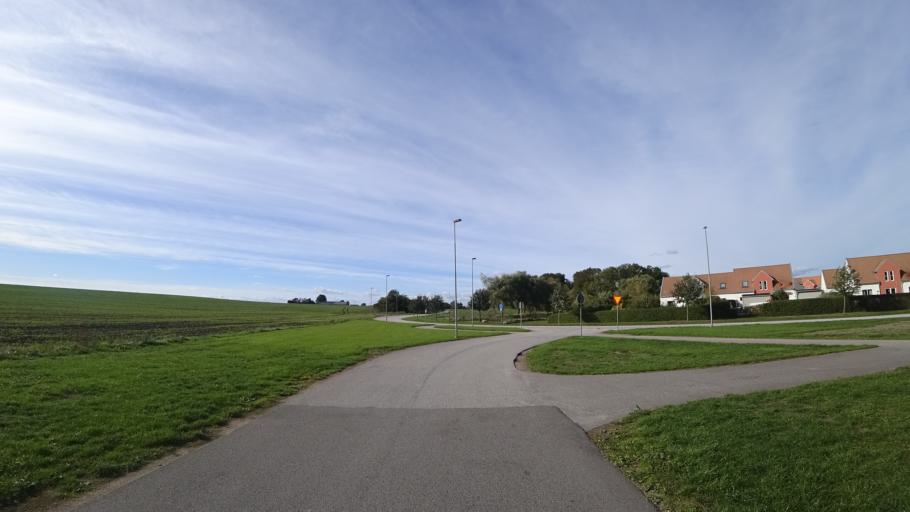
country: SE
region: Skane
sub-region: Kavlinge Kommun
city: Kaevlinge
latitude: 55.8027
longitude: 13.1013
